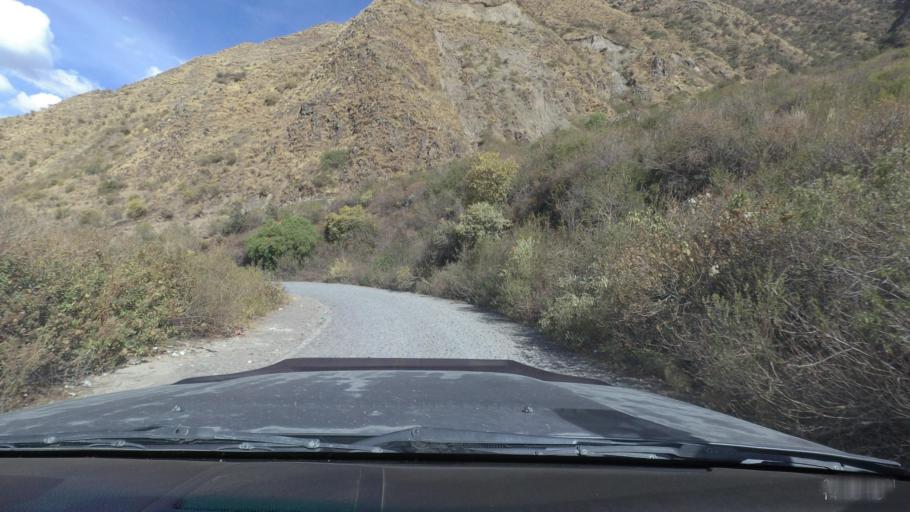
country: BO
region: Cochabamba
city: Sipe Sipe
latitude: -17.2867
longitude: -66.3111
